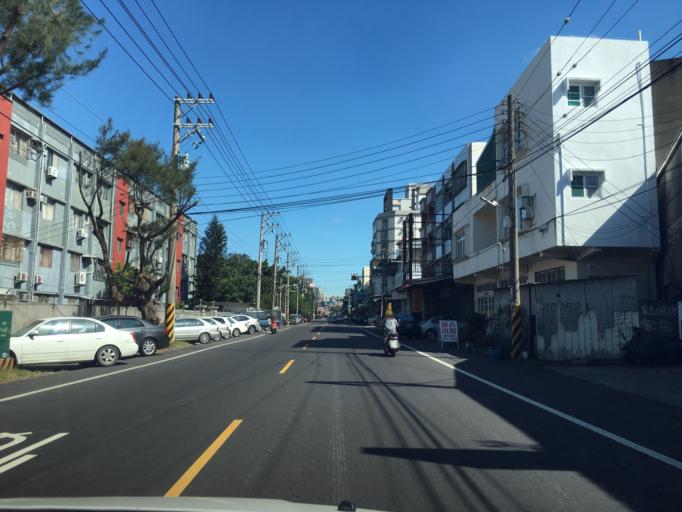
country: TW
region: Taiwan
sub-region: Hsinchu
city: Hsinchu
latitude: 24.8051
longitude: 120.9468
